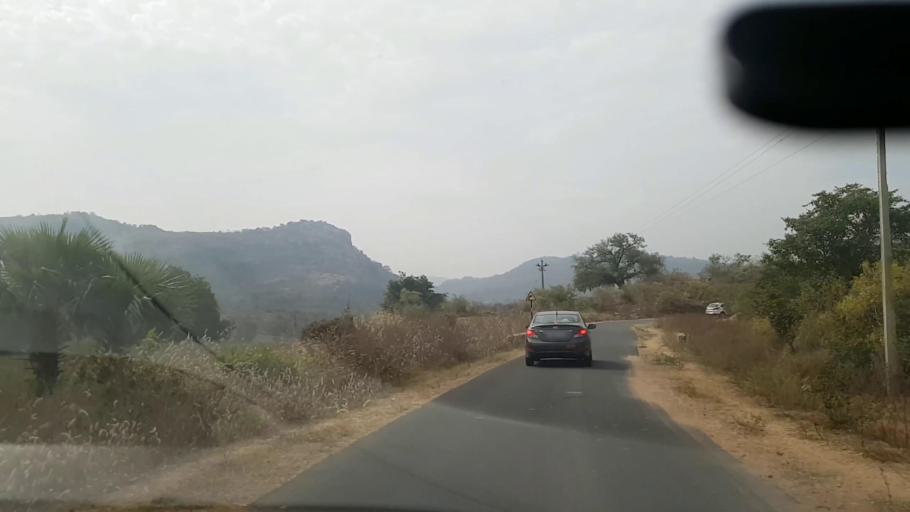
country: IN
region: Telangana
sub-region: Rangareddi
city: Ghatkesar
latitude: 17.1829
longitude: 78.8233
